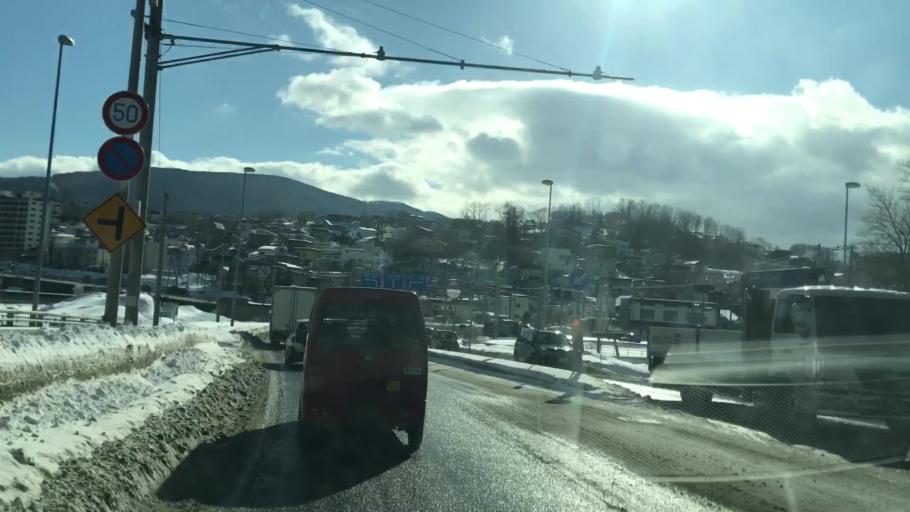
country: JP
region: Hokkaido
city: Otaru
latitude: 43.1796
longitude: 141.0375
